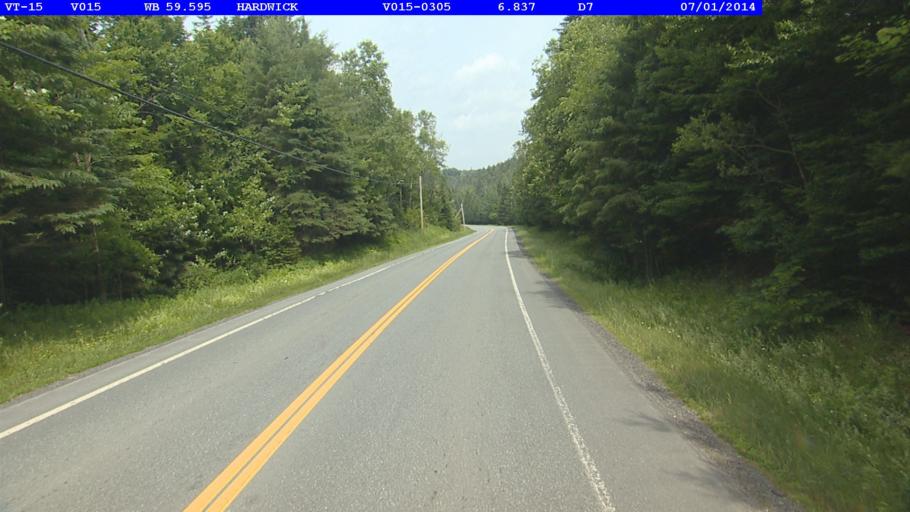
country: US
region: Vermont
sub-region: Caledonia County
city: Hardwick
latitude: 44.4884
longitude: -72.3100
